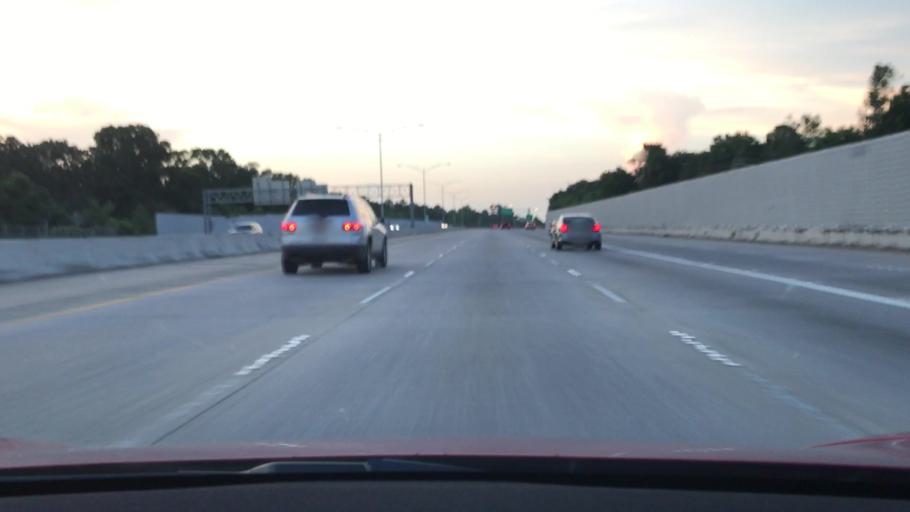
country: US
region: Louisiana
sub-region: Bossier Parish
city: Bossier City
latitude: 32.4585
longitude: -93.7565
